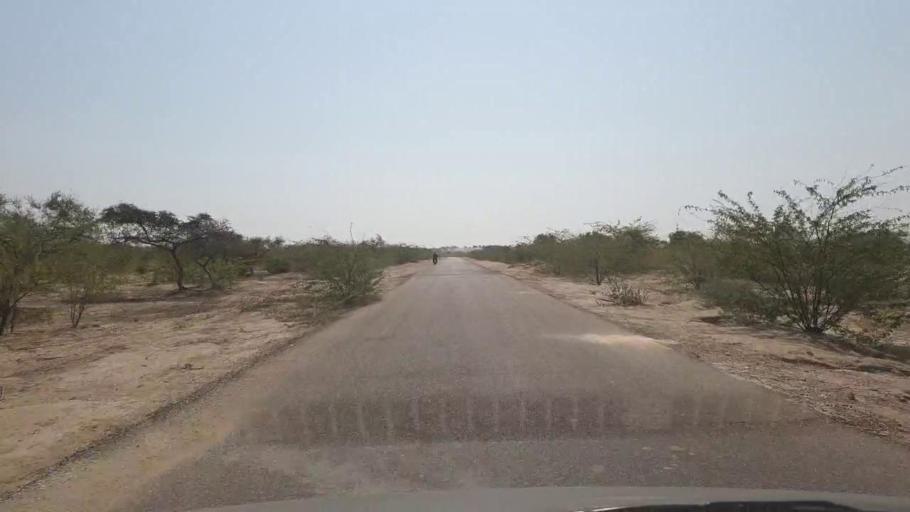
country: PK
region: Sindh
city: Chor
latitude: 25.5916
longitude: 70.1834
